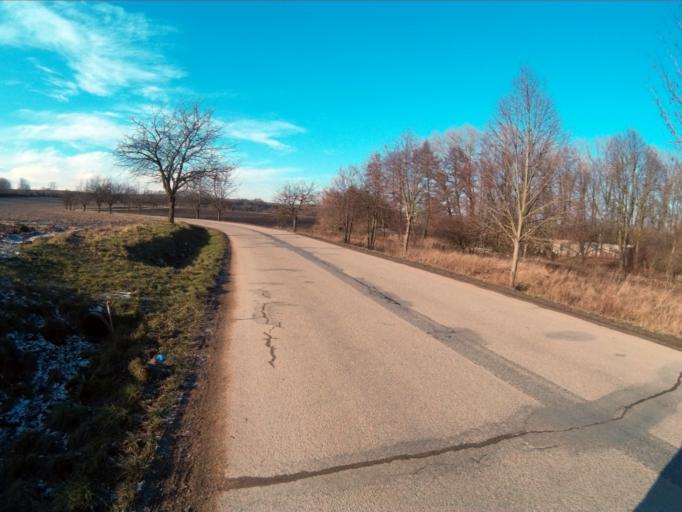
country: CZ
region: South Moravian
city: Krenovice
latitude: 49.1513
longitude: 16.8249
